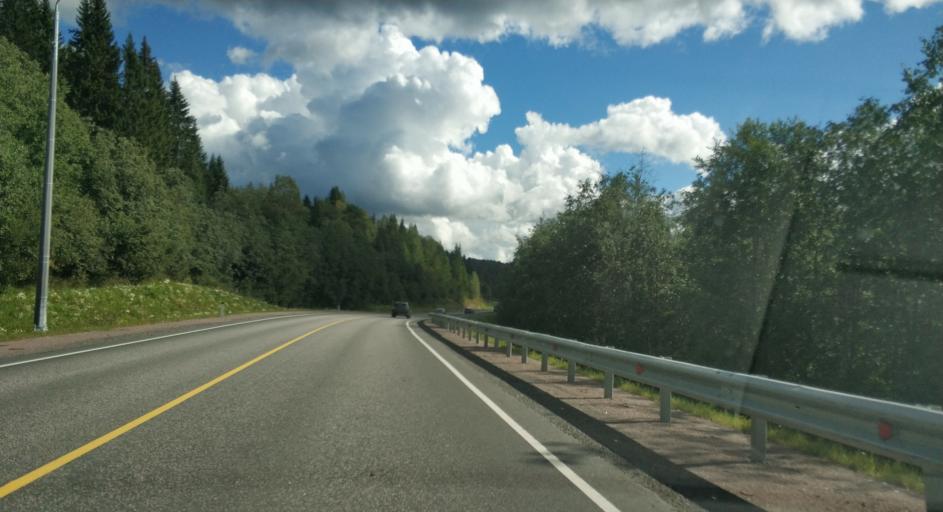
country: RU
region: Republic of Karelia
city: Ruskeala
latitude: 61.9217
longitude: 30.6116
